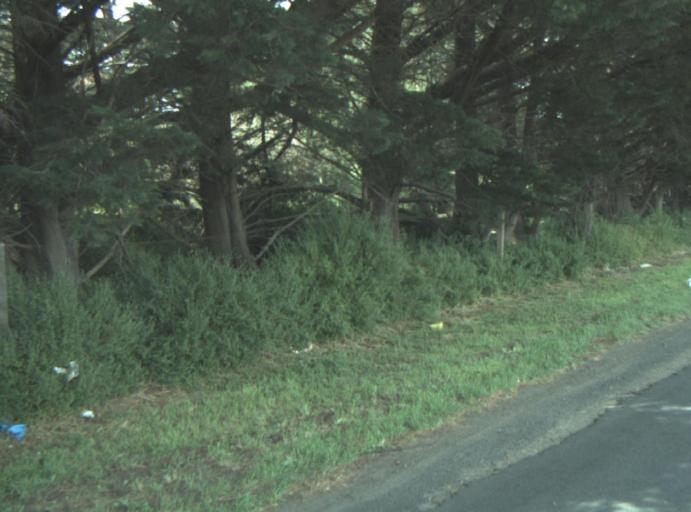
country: AU
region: Victoria
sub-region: Greater Geelong
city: Clifton Springs
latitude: -38.1472
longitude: 144.5962
